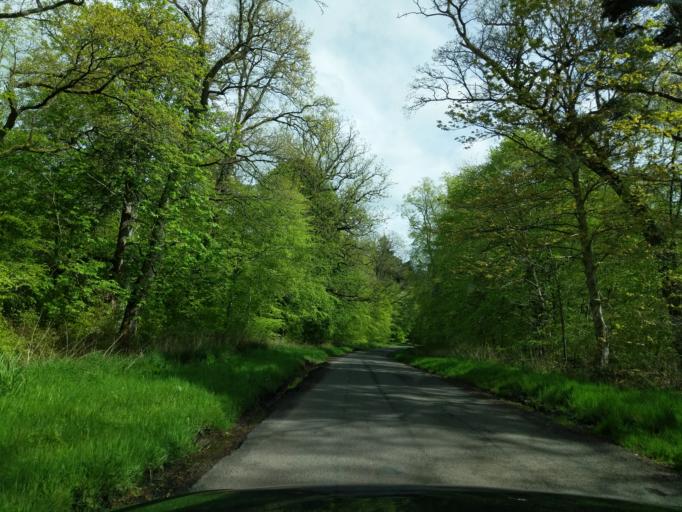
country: GB
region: Scotland
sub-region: The Scottish Borders
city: Saint Boswells
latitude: 55.6512
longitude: -2.5512
